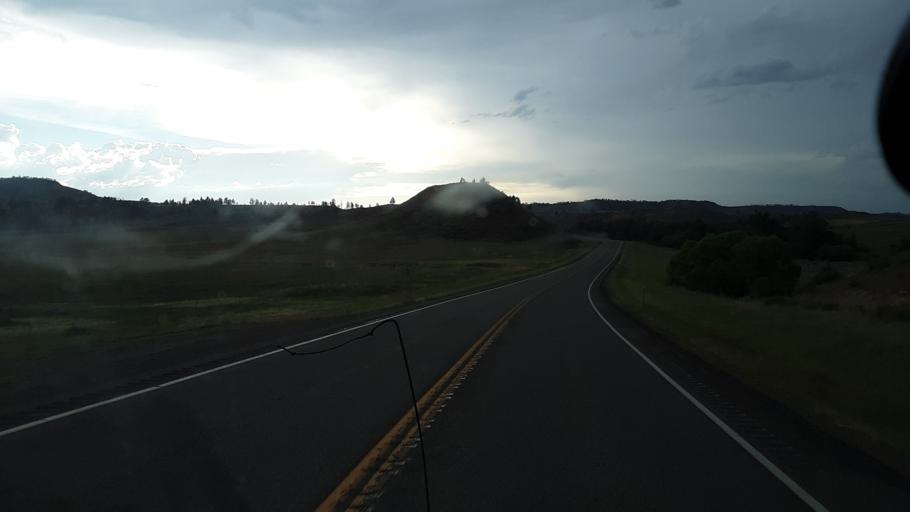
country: US
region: Montana
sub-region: Rosebud County
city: Lame Deer
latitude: 45.6149
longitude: -106.3823
